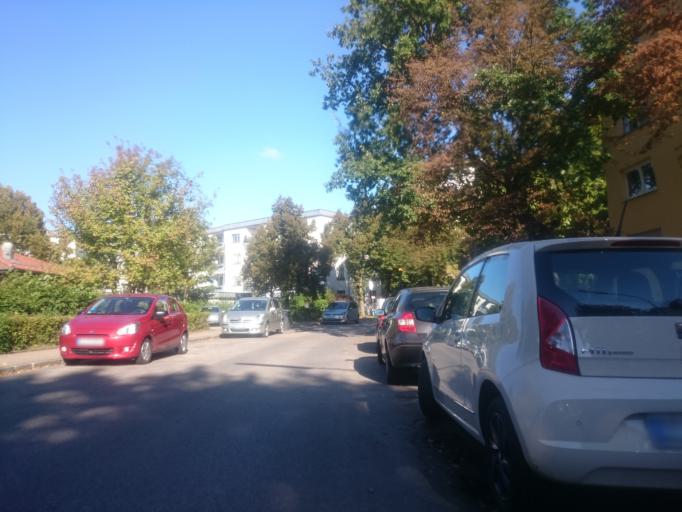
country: DE
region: Bavaria
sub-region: Swabia
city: Augsburg
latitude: 48.3718
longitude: 10.9271
